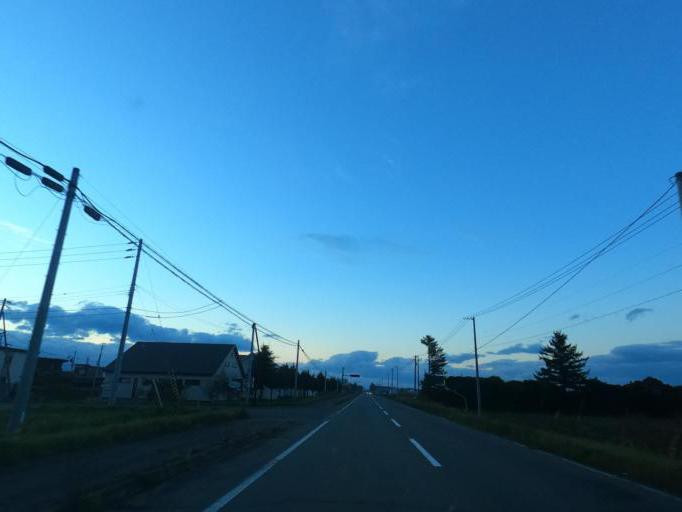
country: JP
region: Hokkaido
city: Obihiro
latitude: 42.6471
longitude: 143.1966
